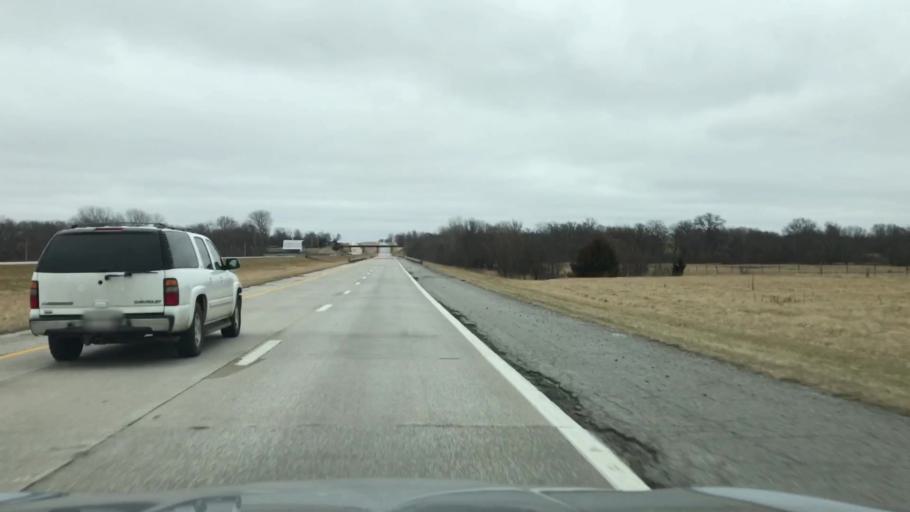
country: US
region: Missouri
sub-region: Linn County
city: Brookfield
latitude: 39.7785
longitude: -93.1526
